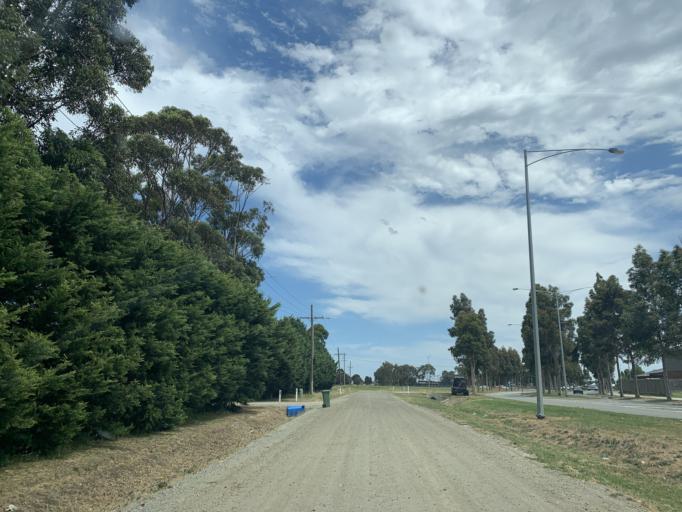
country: AU
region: Victoria
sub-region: Casey
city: Cranbourne East
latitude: -38.1144
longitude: 145.3090
